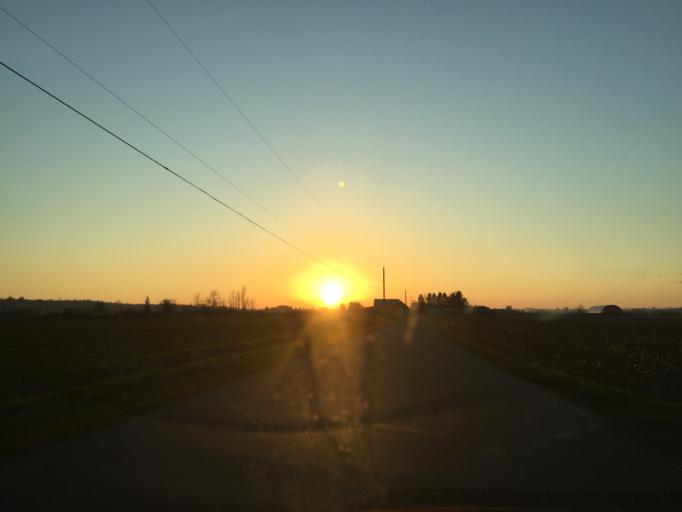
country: US
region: Washington
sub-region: Whatcom County
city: Sumas
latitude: 48.9827
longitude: -122.2097
